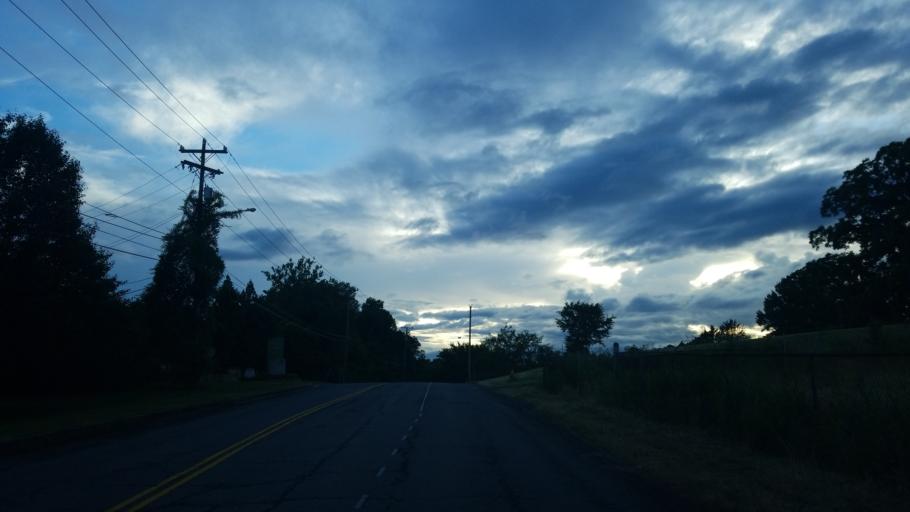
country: US
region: Tennessee
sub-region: Rutherford County
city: La Vergne
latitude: 36.1130
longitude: -86.6406
